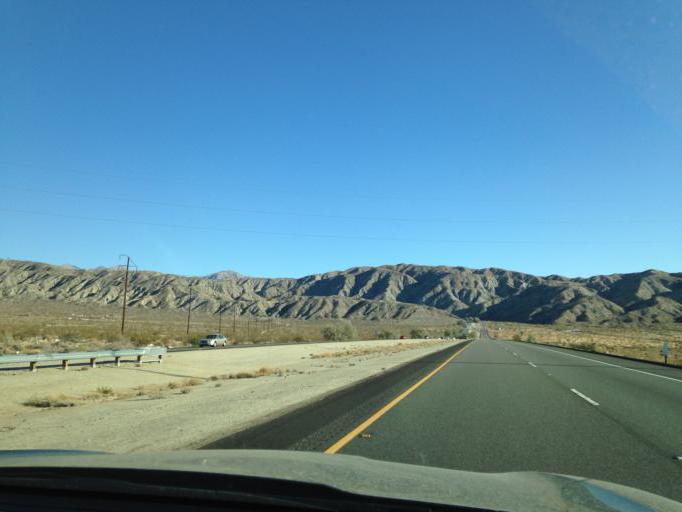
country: US
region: California
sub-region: San Bernardino County
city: Morongo Valley
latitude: 33.9938
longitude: -116.5799
